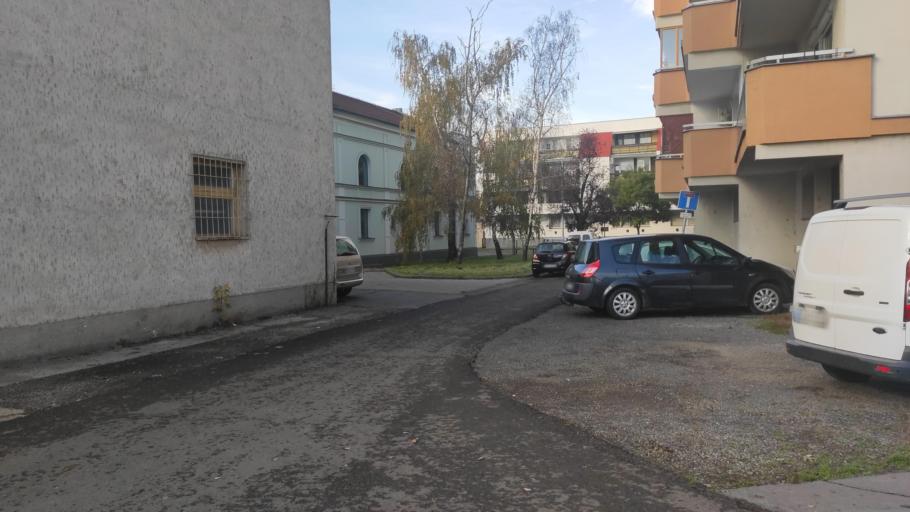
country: HU
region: Bekes
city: Bekes
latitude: 46.7709
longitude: 21.1294
